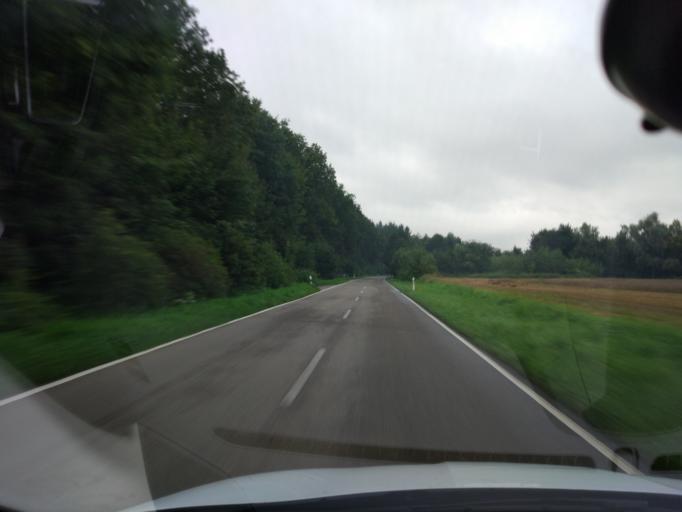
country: DE
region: Baden-Wuerttemberg
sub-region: Tuebingen Region
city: Huttisheim
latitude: 48.3164
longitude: 9.9388
